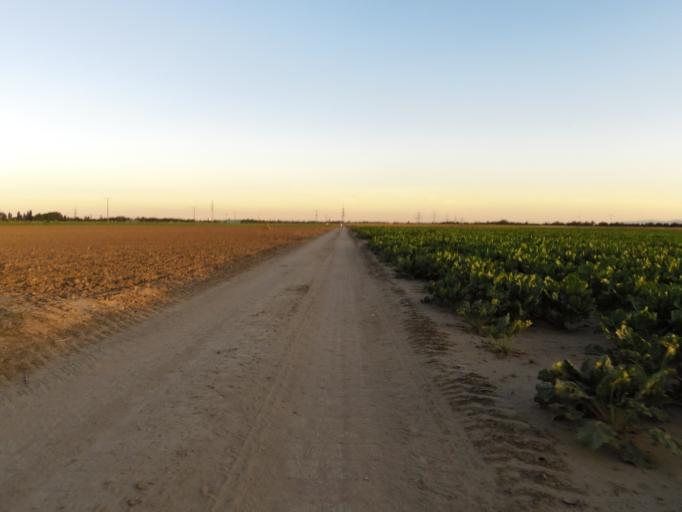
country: DE
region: Rheinland-Pfalz
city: Bobenheim-Roxheim
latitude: 49.5744
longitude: 8.3467
